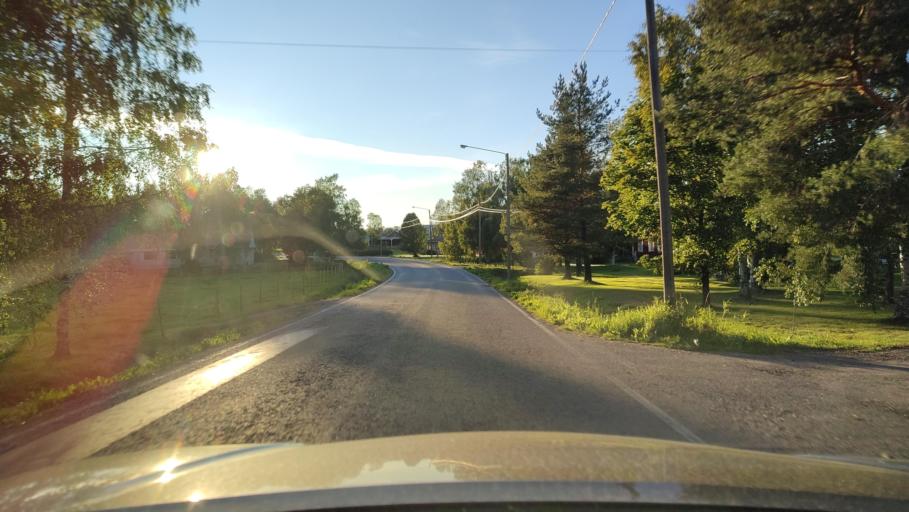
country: FI
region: Ostrobothnia
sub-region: Sydosterbotten
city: Kristinestad
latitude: 62.2487
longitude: 21.5361
